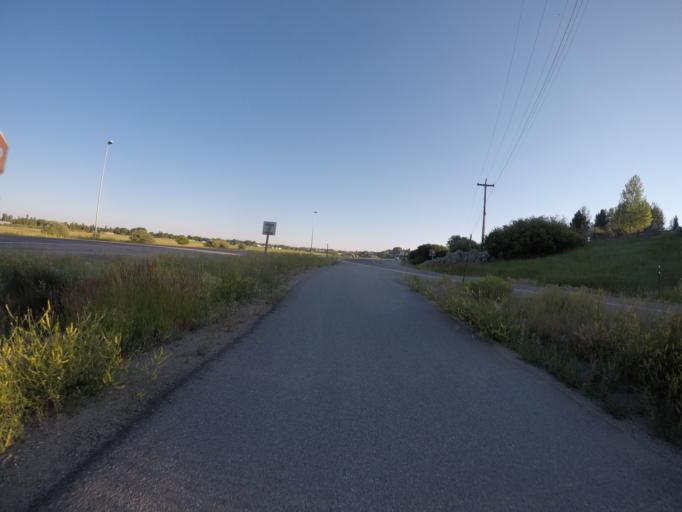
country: US
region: Wyoming
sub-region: Sublette County
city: Pinedale
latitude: 42.8559
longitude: -109.8501
